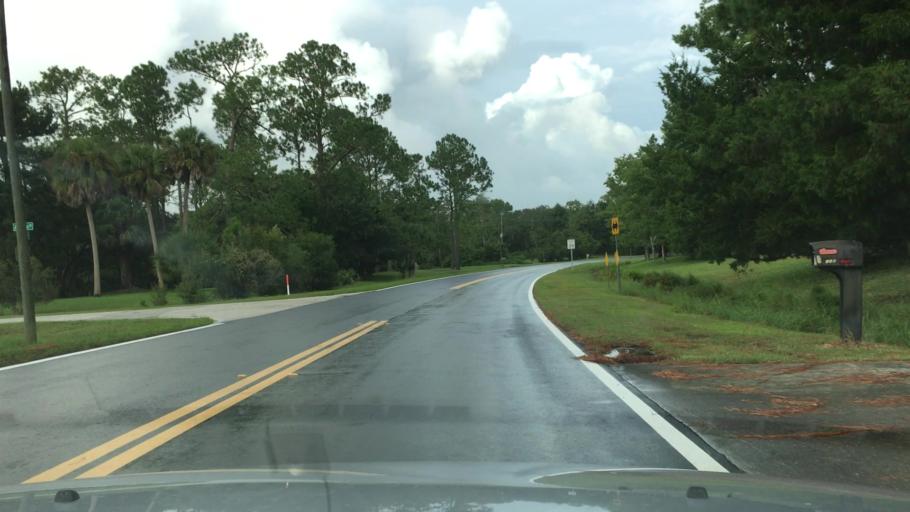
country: US
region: Florida
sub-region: Volusia County
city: Ormond-by-the-Sea
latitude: 29.3321
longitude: -81.1142
